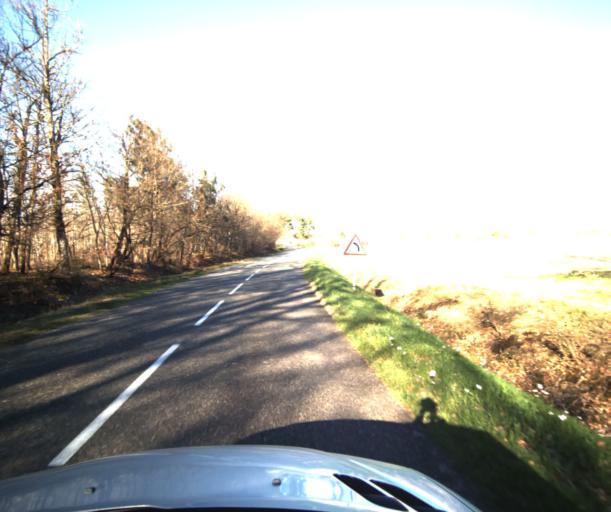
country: FR
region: Midi-Pyrenees
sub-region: Departement du Tarn-et-Garonne
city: Campsas
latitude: 43.9328
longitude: 1.2957
